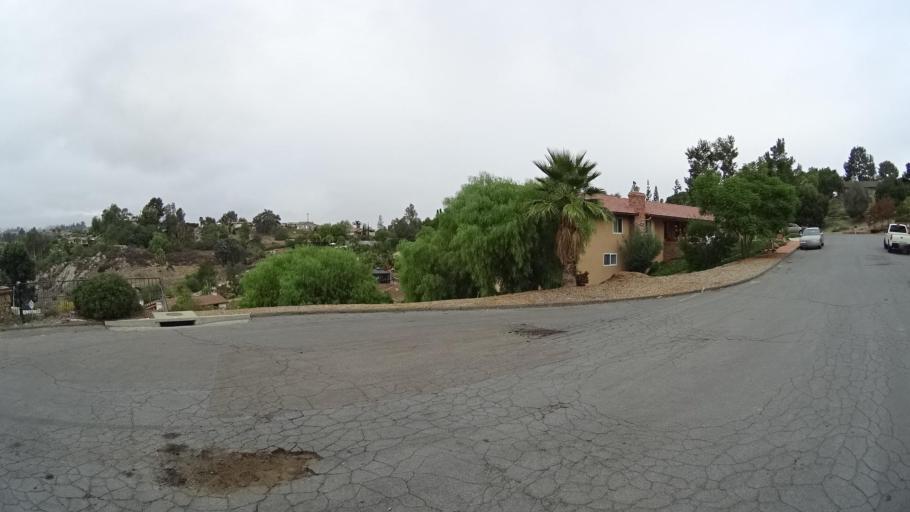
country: US
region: California
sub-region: San Diego County
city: Rancho San Diego
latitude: 32.7706
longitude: -116.9155
